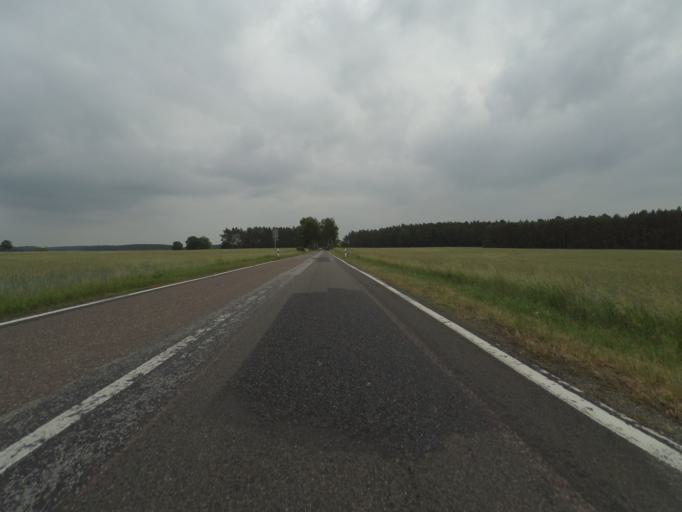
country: DE
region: Mecklenburg-Vorpommern
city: Siggelkow
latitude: 53.3723
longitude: 11.9957
